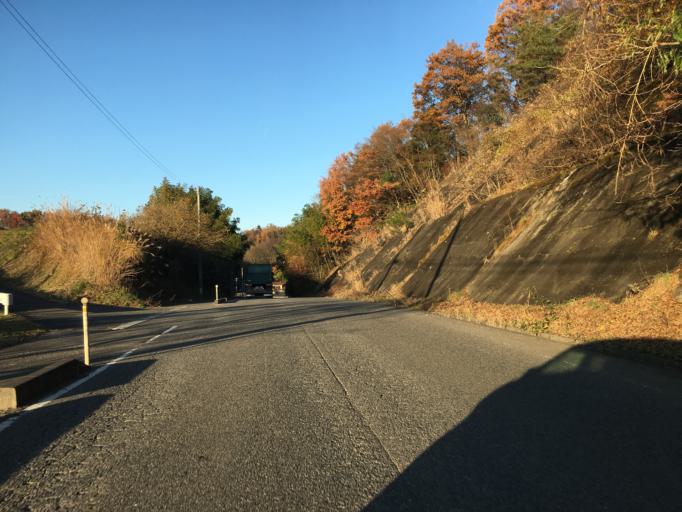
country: JP
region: Fukushima
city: Miharu
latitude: 37.4481
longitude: 140.4440
